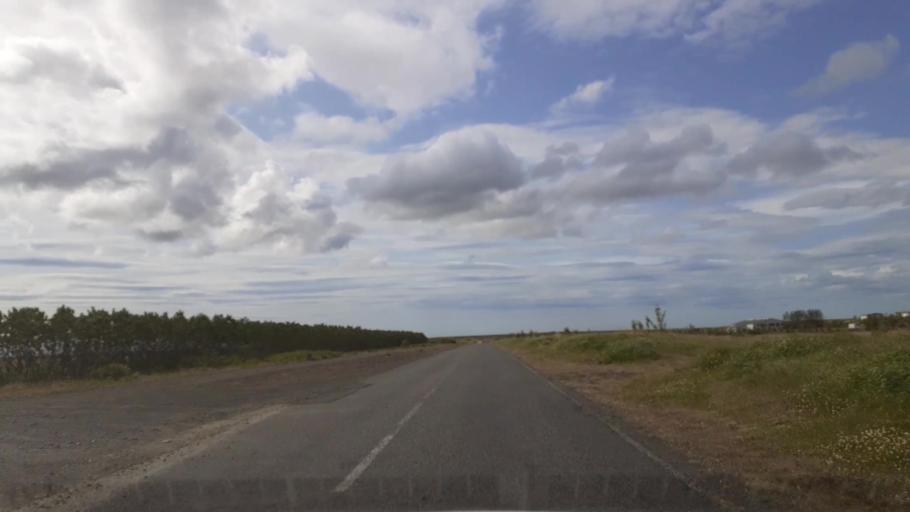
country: IS
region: South
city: Vestmannaeyjar
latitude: 63.8291
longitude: -20.4024
